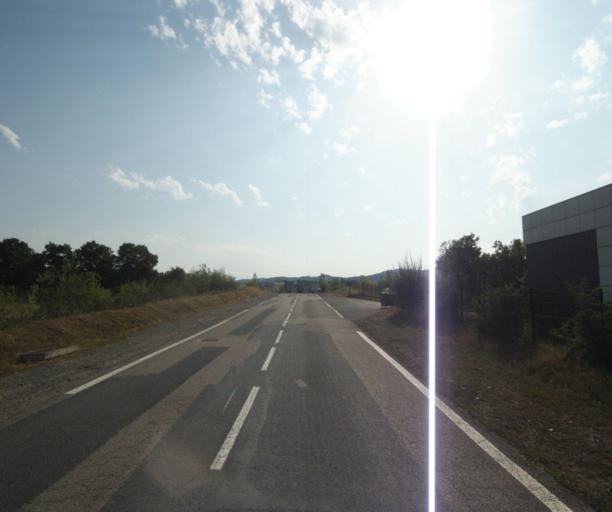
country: FR
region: Rhone-Alpes
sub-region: Departement du Rhone
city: Sain-Bel
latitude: 45.8233
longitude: 4.5957
